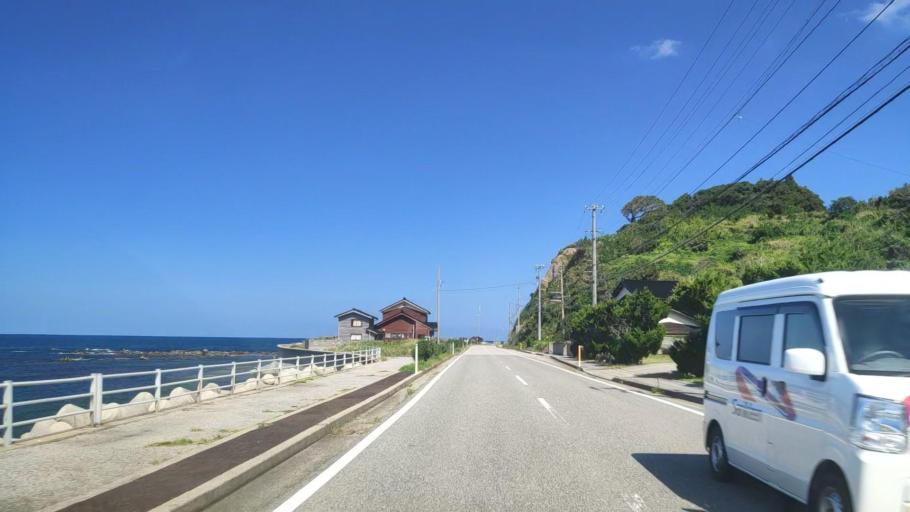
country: JP
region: Ishikawa
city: Nanao
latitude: 37.4870
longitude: 137.1181
